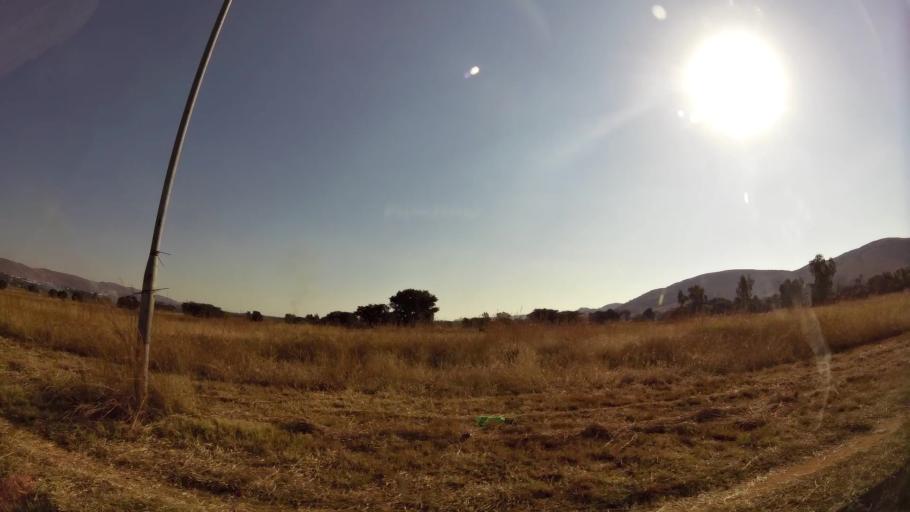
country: ZA
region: Gauteng
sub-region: City of Tshwane Metropolitan Municipality
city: Pretoria
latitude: -25.6978
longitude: 28.1391
